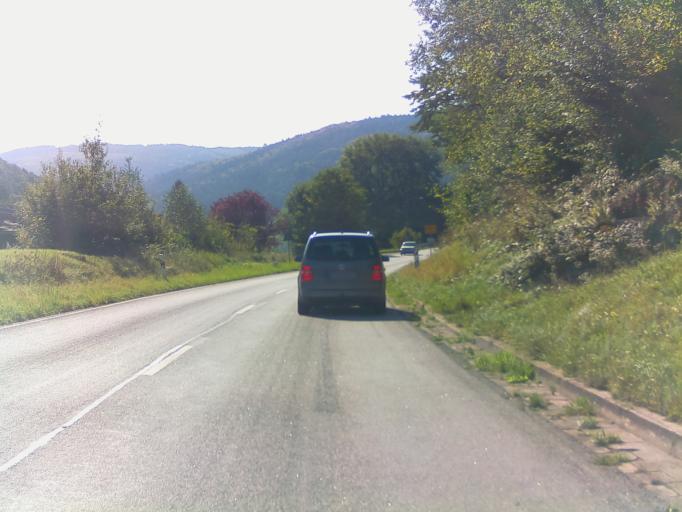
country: DE
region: Baden-Wuerttemberg
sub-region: Karlsruhe Region
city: Heddesbach
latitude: 49.4861
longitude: 8.8287
